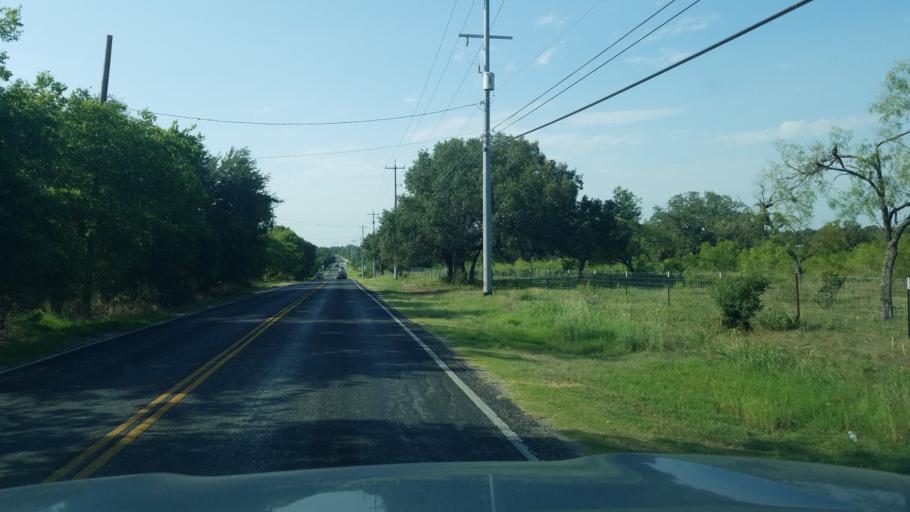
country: US
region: Texas
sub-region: Bexar County
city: Helotes
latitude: 29.4513
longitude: -98.7543
